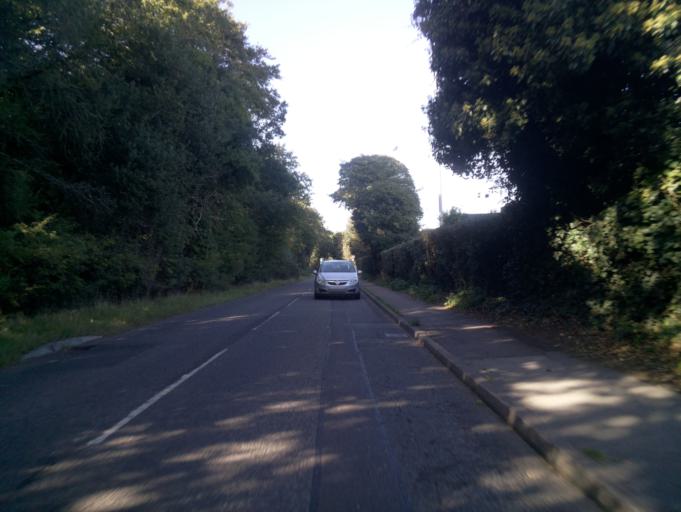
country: GB
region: England
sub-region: West Berkshire
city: Cold Ash
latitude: 51.4330
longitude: -1.2696
